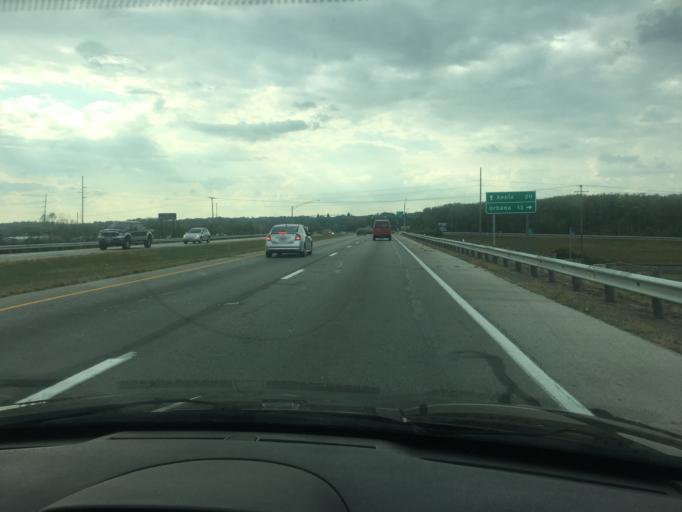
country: US
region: Ohio
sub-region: Clark County
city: Springfield
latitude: 39.9425
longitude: -83.8381
